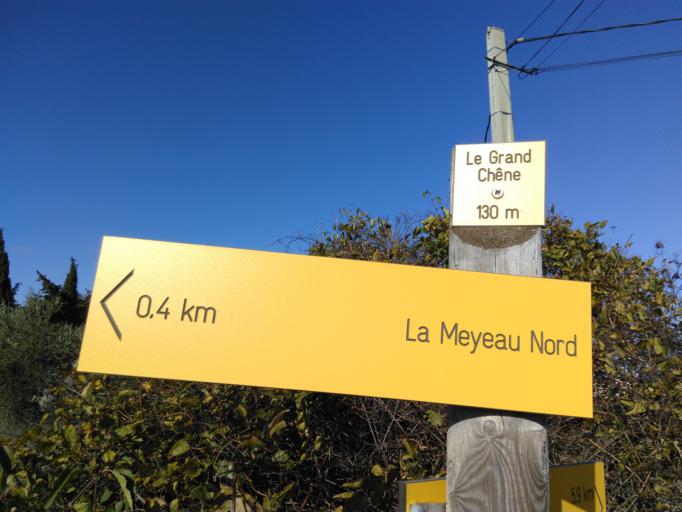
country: FR
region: Provence-Alpes-Cote d'Azur
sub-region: Departement du Vaucluse
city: Violes
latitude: 44.2228
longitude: 4.9490
